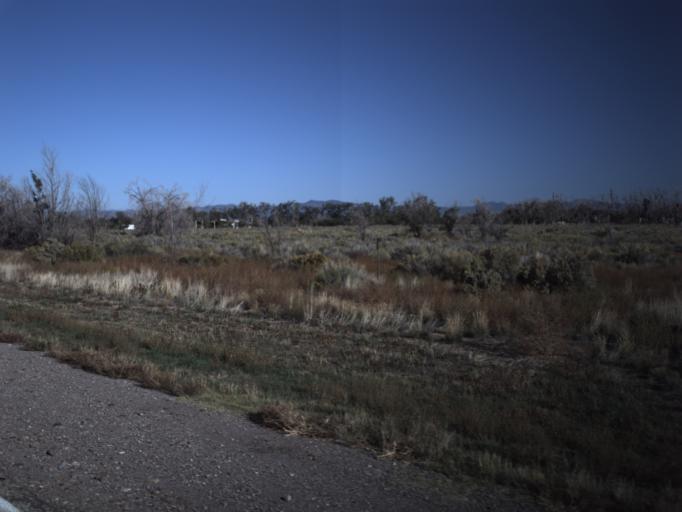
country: US
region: Utah
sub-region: Washington County
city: Enterprise
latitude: 37.7097
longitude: -113.6568
